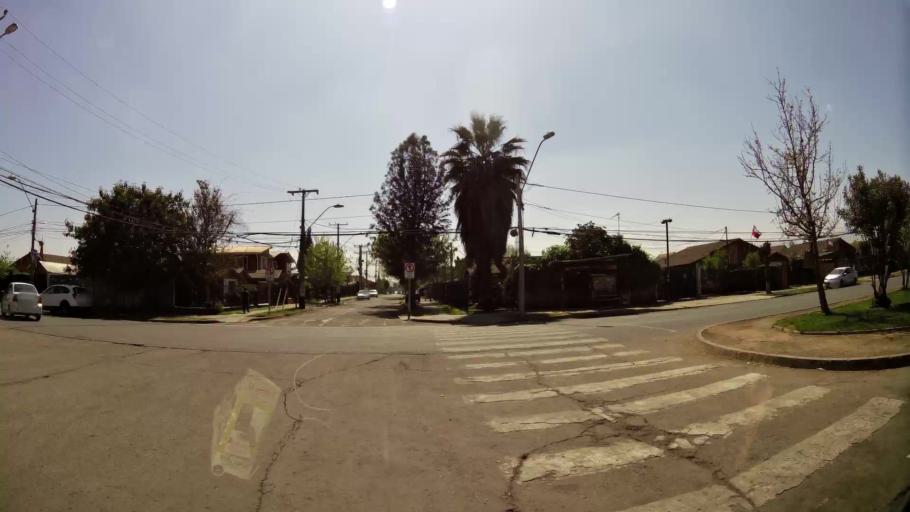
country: CL
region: Santiago Metropolitan
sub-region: Provincia de Santiago
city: Lo Prado
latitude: -33.3578
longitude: -70.7321
